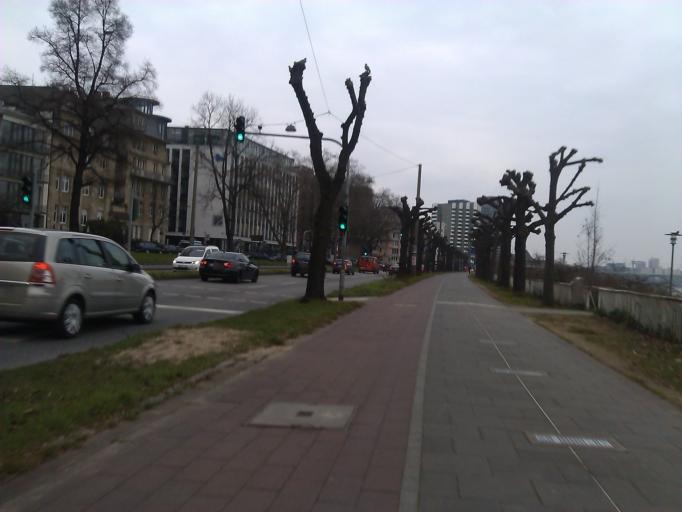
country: DE
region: North Rhine-Westphalia
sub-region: Regierungsbezirk Koln
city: Altstadt Nord
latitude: 50.9467
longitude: 6.9641
